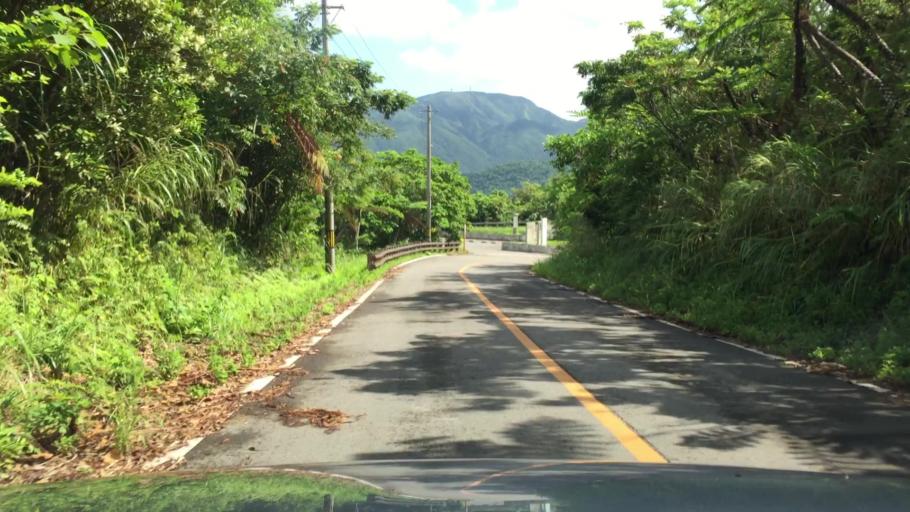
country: JP
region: Okinawa
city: Ishigaki
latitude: 24.3836
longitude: 124.1666
